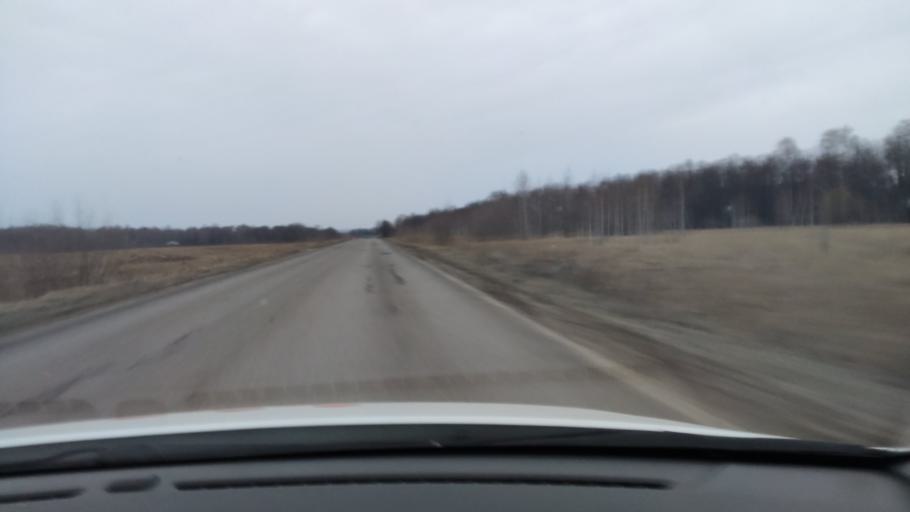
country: RU
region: Tatarstan
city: Stolbishchi
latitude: 55.7146
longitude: 49.1725
